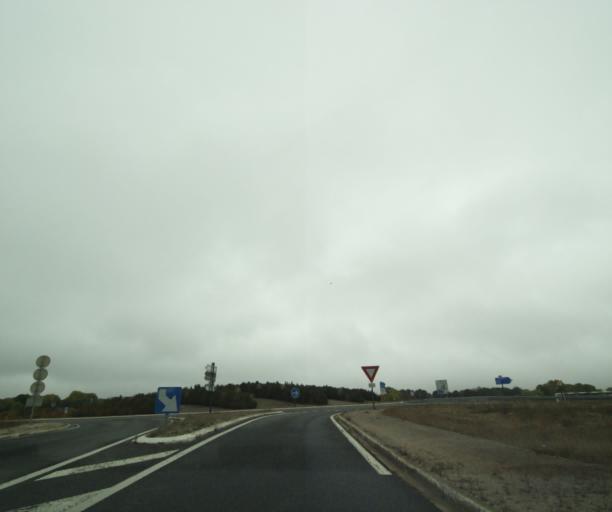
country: FR
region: Midi-Pyrenees
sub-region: Departement de l'Aveyron
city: La Cavalerie
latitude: 44.0129
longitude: 3.1416
